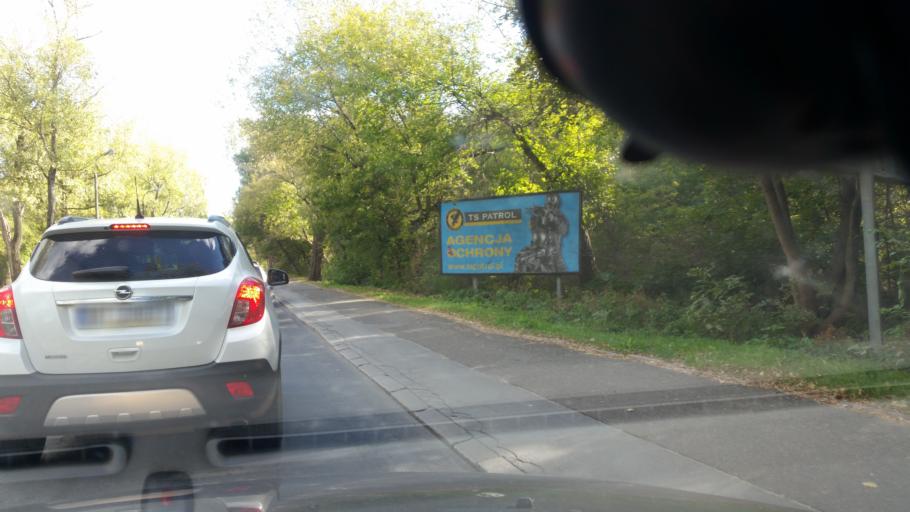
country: PL
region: Masovian Voivodeship
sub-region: Warszawa
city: Praga Polnoc
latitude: 52.2603
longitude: 21.0162
